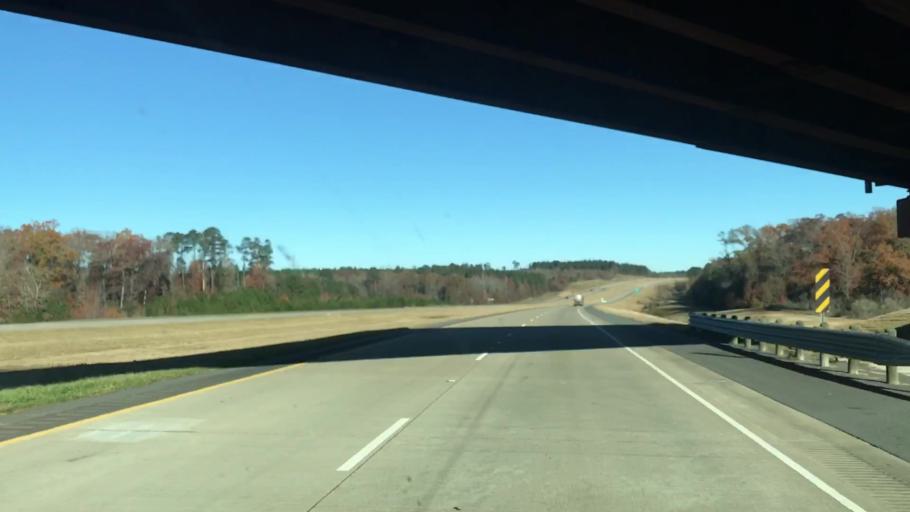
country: US
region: Louisiana
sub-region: Caddo Parish
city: Vivian
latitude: 32.9786
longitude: -93.9096
